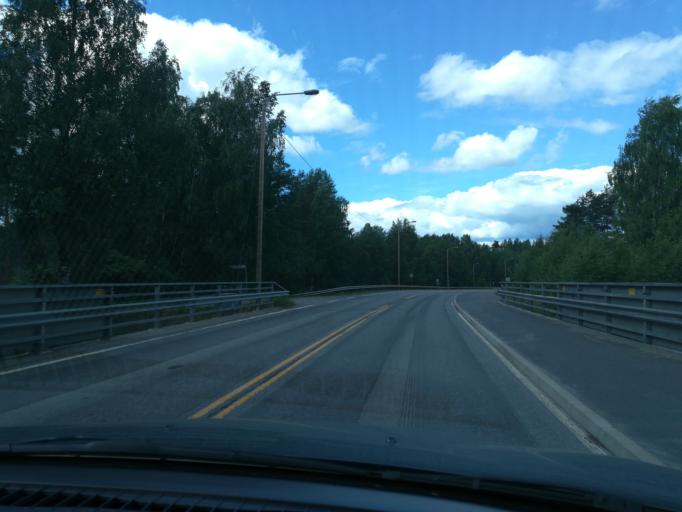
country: FI
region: Southern Savonia
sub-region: Mikkeli
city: Maentyharju
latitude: 61.4352
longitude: 26.8789
